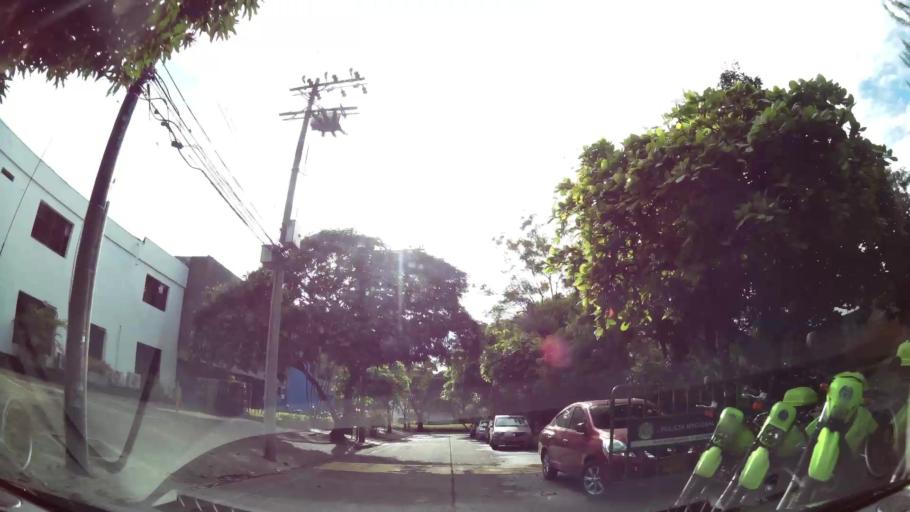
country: CO
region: Valle del Cauca
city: Cali
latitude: 3.4821
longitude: -76.5222
